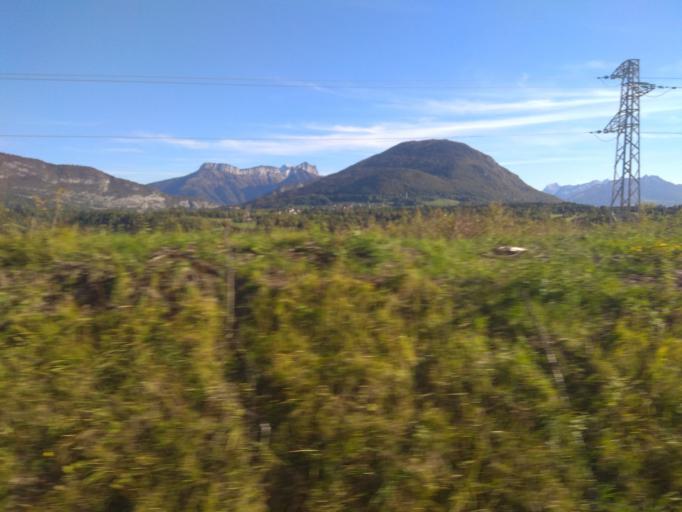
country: FR
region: Rhone-Alpes
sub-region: Departement de la Haute-Savoie
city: Saint-Martin-Bellevue
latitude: 45.9444
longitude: 6.1524
